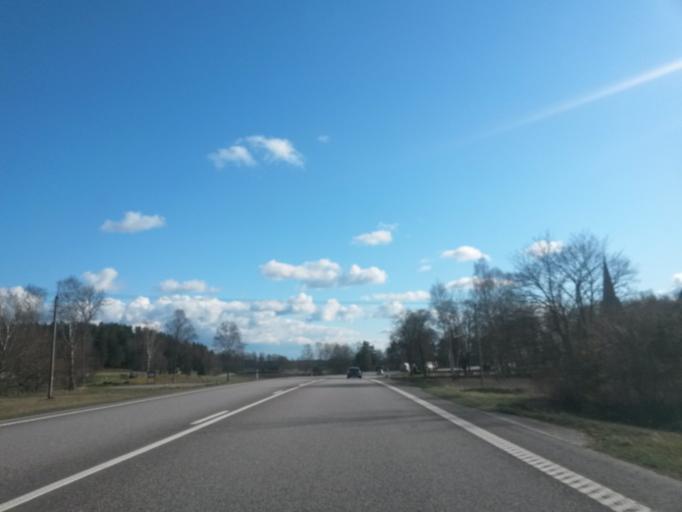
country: SE
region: Vaestra Goetaland
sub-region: Vargarda Kommun
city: Vargarda
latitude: 58.0941
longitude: 12.8300
